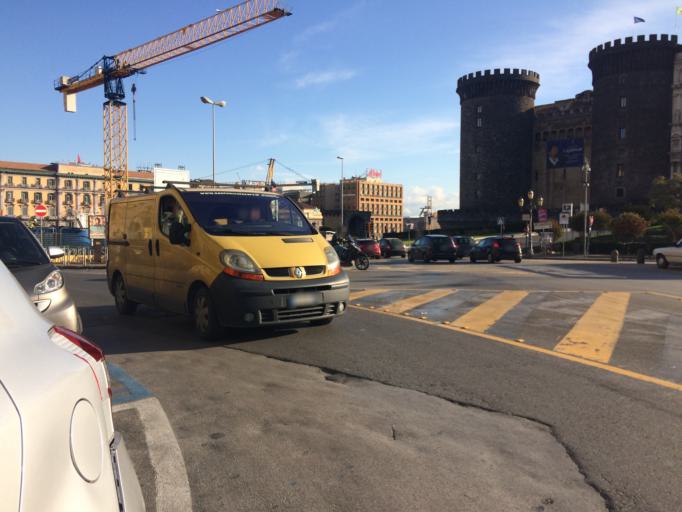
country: IT
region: Campania
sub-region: Provincia di Napoli
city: Napoli
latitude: 40.8385
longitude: 14.2512
